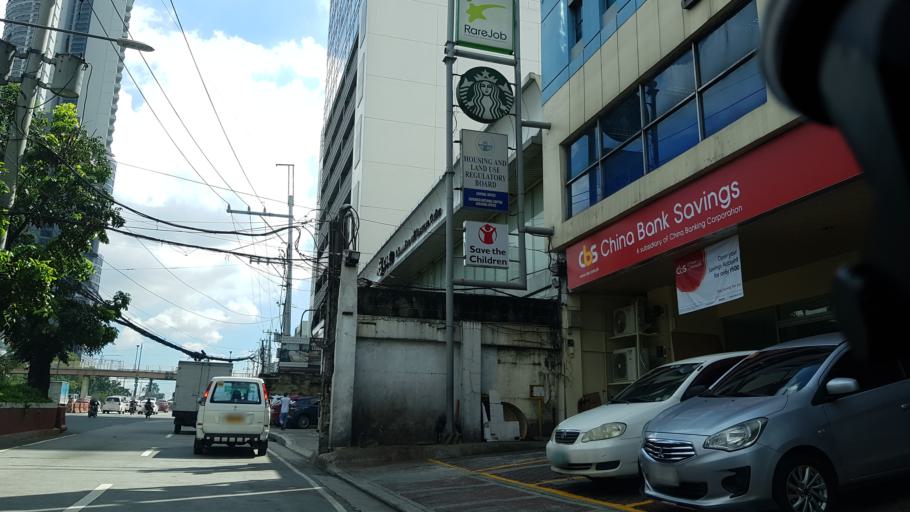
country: PH
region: Calabarzon
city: Del Monte
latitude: 14.6420
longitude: 121.0344
